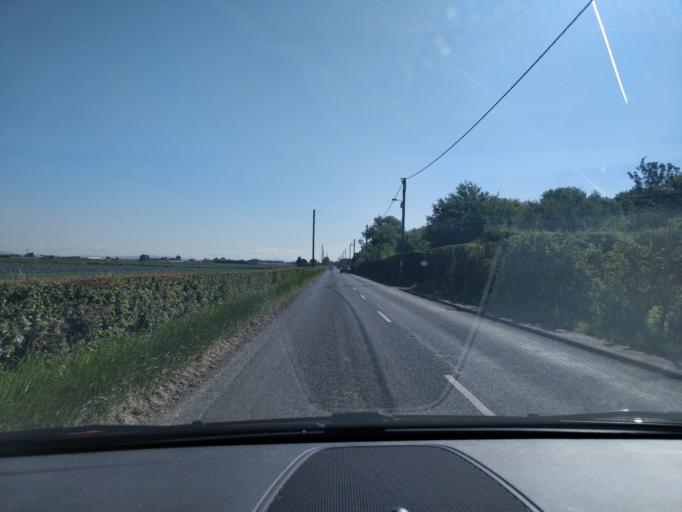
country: GB
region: England
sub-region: Lancashire
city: Tarleton
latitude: 53.7059
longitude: -2.8616
